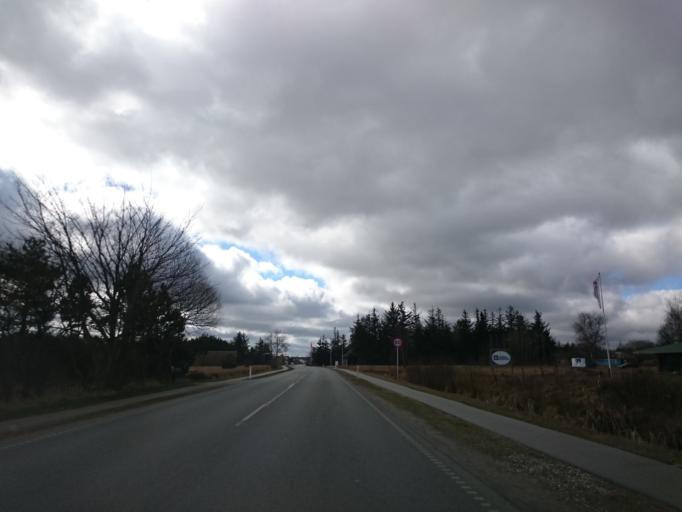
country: DK
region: North Denmark
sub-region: Frederikshavn Kommune
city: Strandby
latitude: 57.6000
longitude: 10.4185
